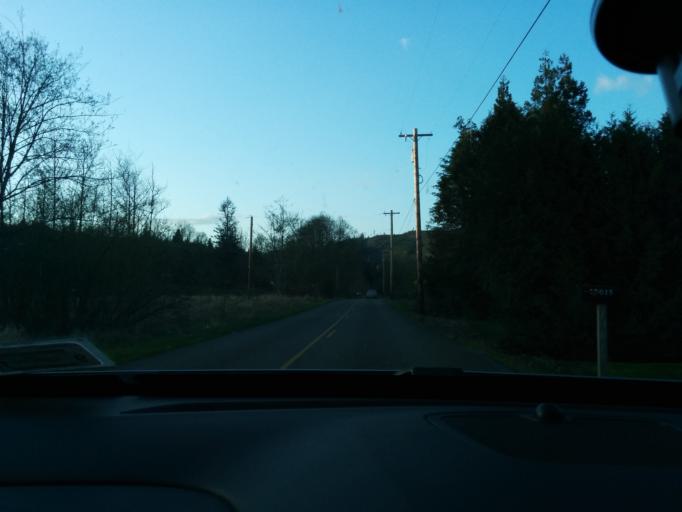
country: US
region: Washington
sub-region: Snohomish County
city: Gold Bar
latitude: 47.8802
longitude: -121.7344
